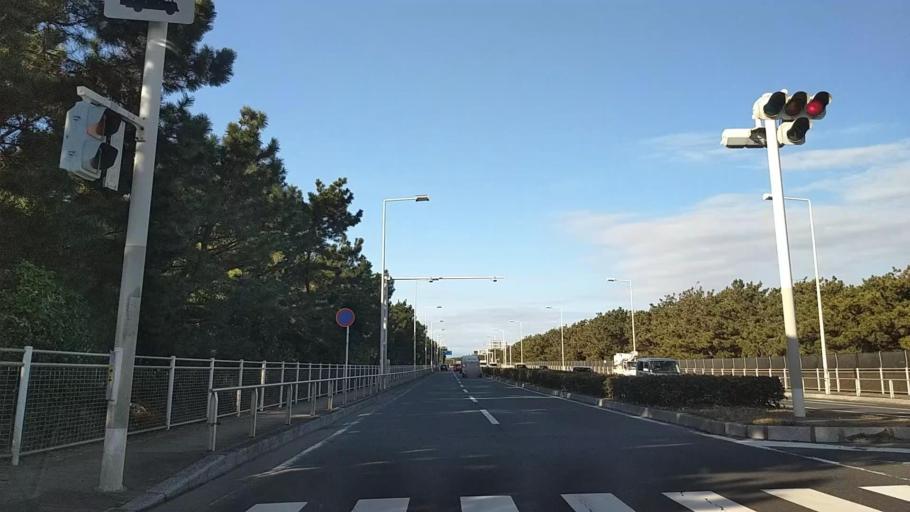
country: JP
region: Kanagawa
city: Chigasaki
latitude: 35.3200
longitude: 139.4323
